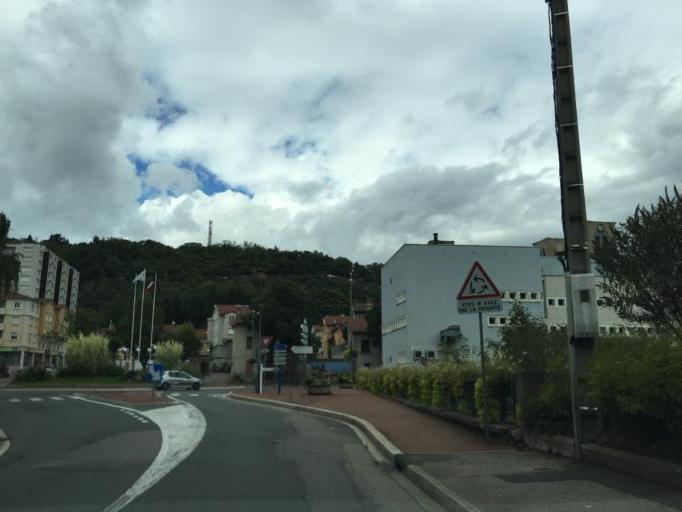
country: FR
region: Rhone-Alpes
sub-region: Departement de la Loire
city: Rive-de-Gier
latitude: 45.5303
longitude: 4.6233
